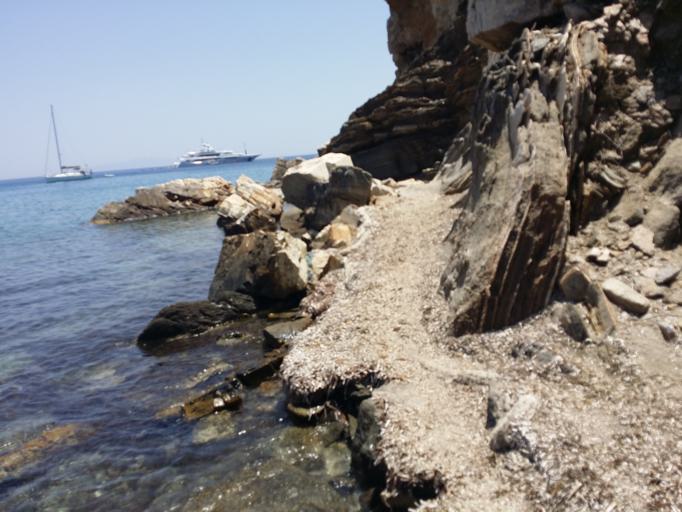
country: GR
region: South Aegean
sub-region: Nomos Kykladon
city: Antiparos
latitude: 36.9547
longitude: 24.9994
